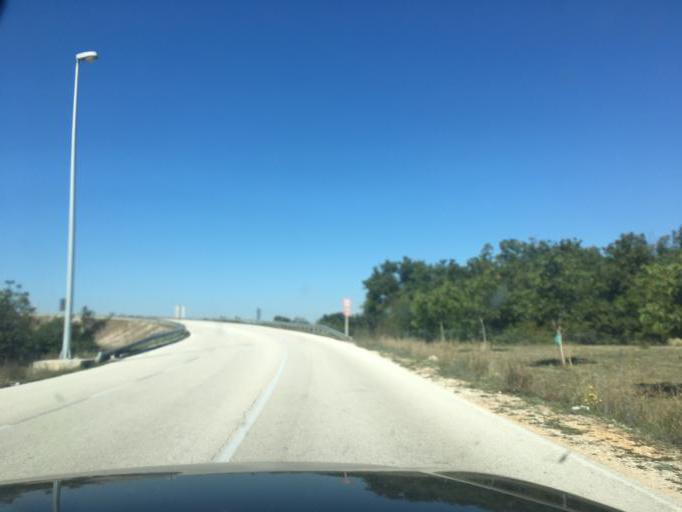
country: HR
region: Splitsko-Dalmatinska
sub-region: Grad Trogir
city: Trogir
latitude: 43.6124
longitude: 16.2287
